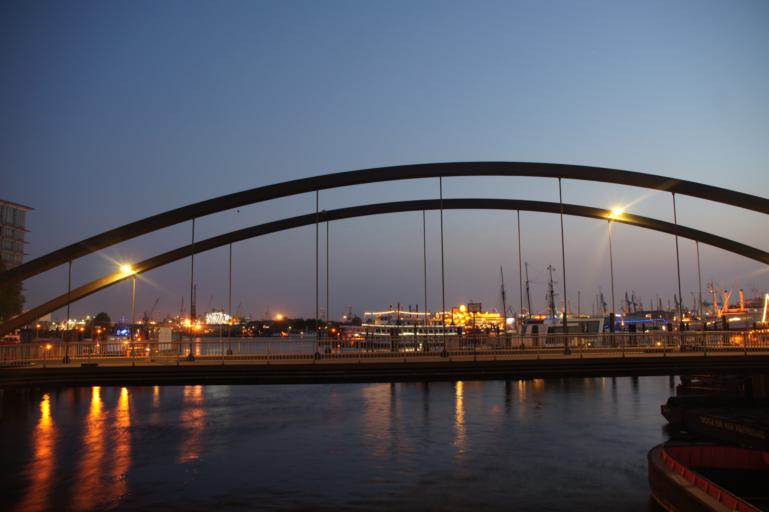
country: DE
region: Hamburg
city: Neustadt
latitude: 53.5441
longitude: 9.9825
